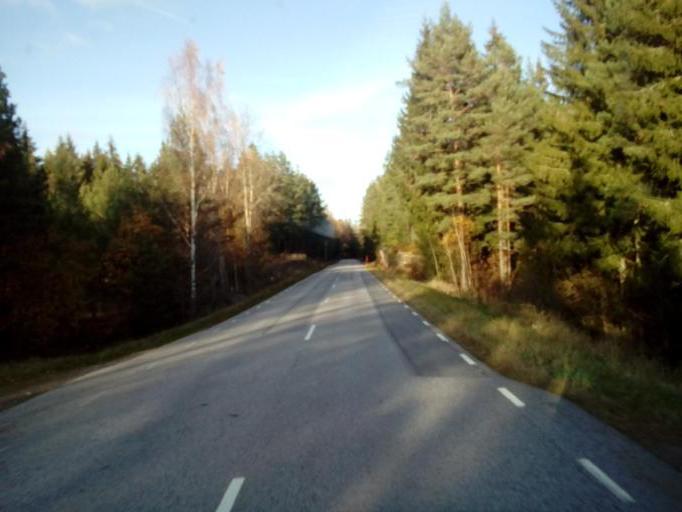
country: SE
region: Kalmar
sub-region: Vasterviks Kommun
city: Ankarsrum
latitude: 57.7464
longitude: 16.1125
